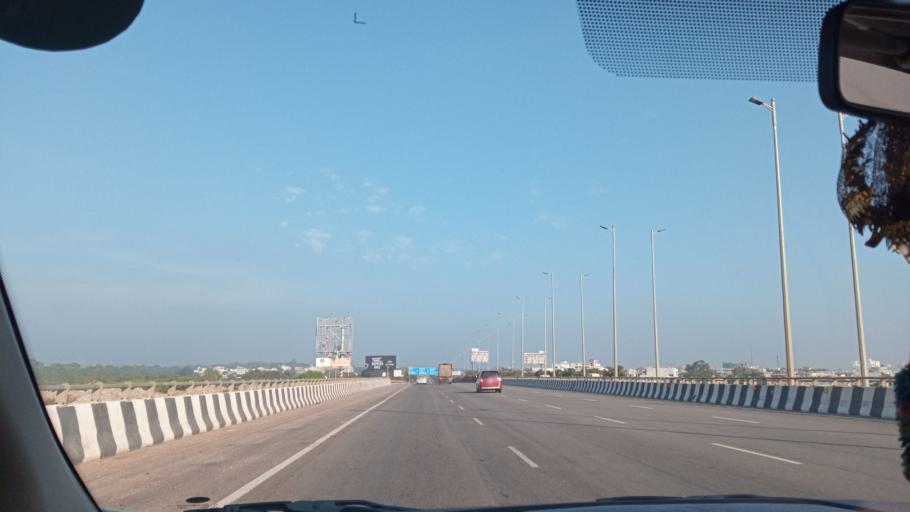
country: IN
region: Telangana
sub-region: Hyderabad
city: Hyderabad
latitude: 17.3277
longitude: 78.3730
